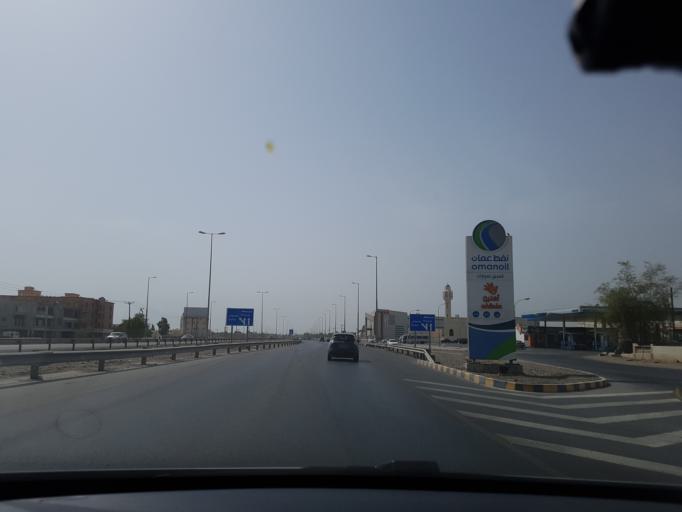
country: OM
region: Al Batinah
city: Al Khaburah
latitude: 23.9656
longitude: 57.0953
